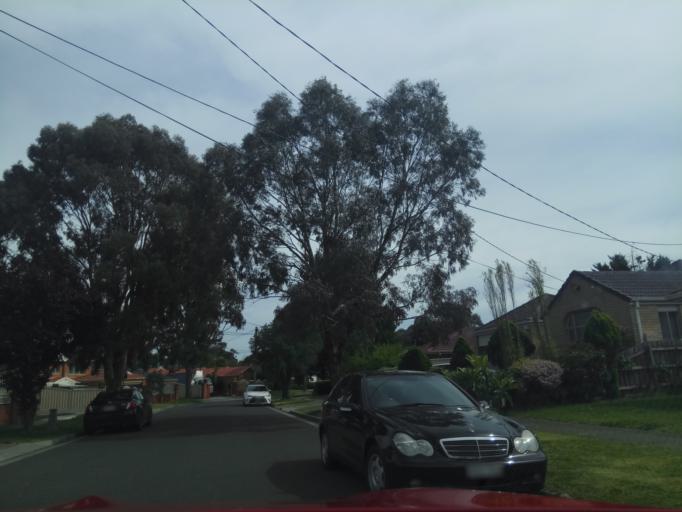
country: AU
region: Victoria
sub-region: Greater Dandenong
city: Springvale South
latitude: -37.9676
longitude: 145.1374
